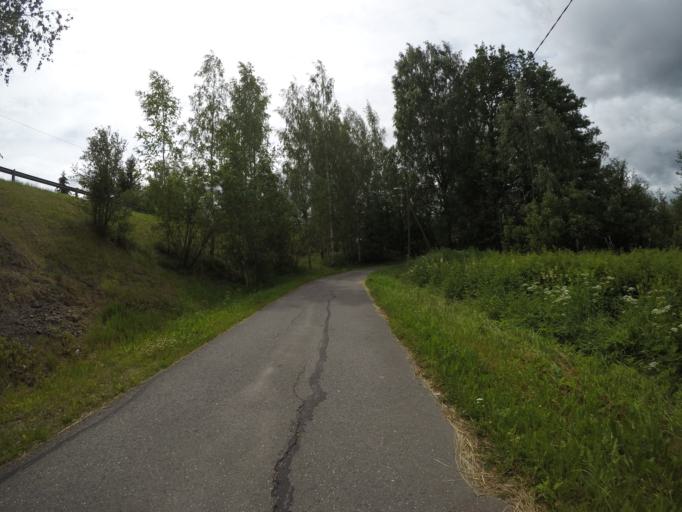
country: FI
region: Haeme
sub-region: Haemeenlinna
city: Haemeenlinna
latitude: 60.9995
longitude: 24.4991
